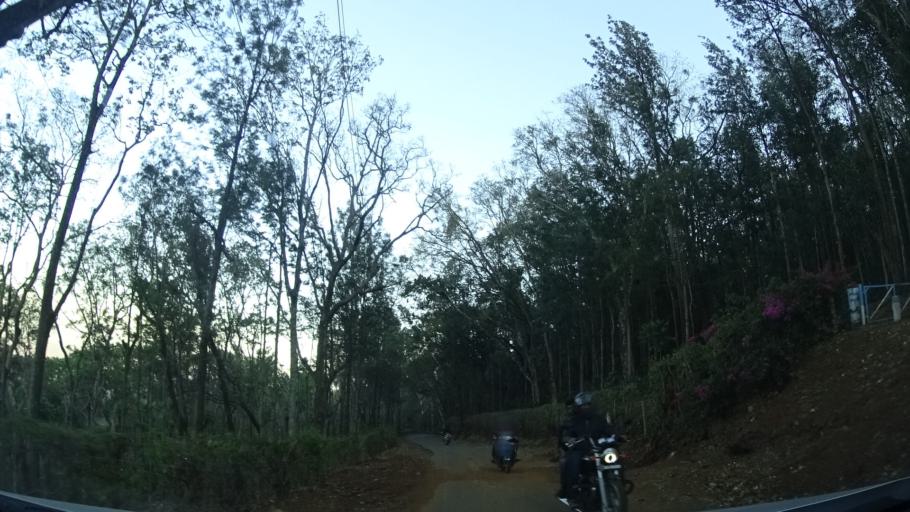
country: IN
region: Karnataka
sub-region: Chikmagalur
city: Tarikere
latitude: 13.5642
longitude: 75.7731
